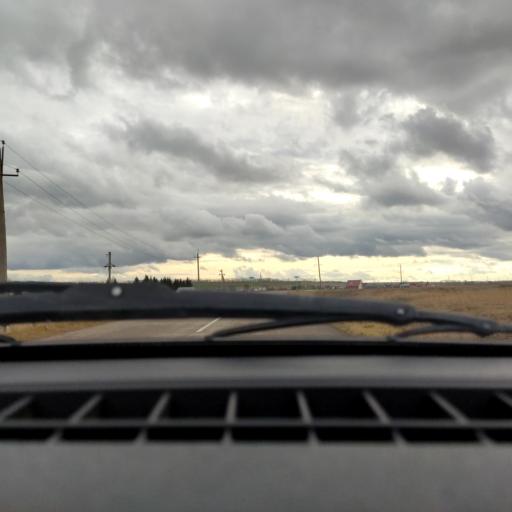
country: RU
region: Bashkortostan
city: Asanovo
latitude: 54.9303
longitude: 55.5187
